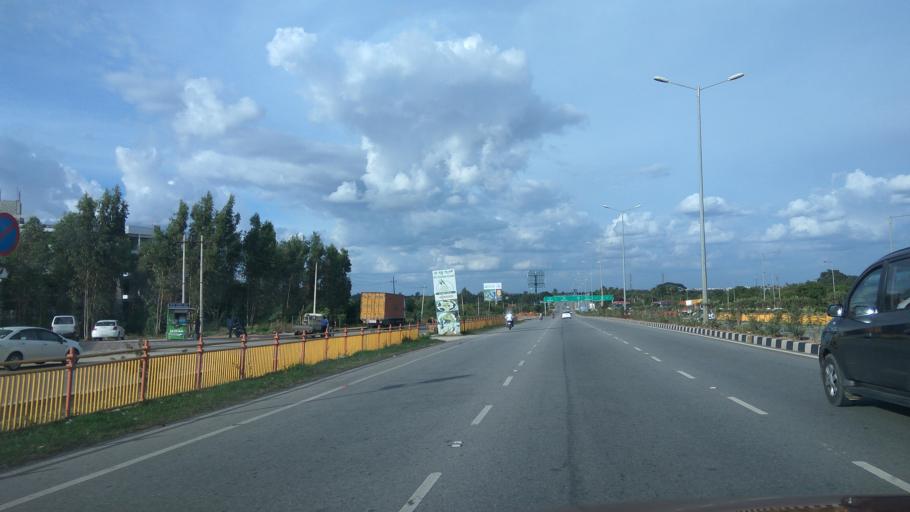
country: IN
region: Karnataka
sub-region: Bangalore Rural
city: Devanhalli
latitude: 13.2094
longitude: 77.6704
